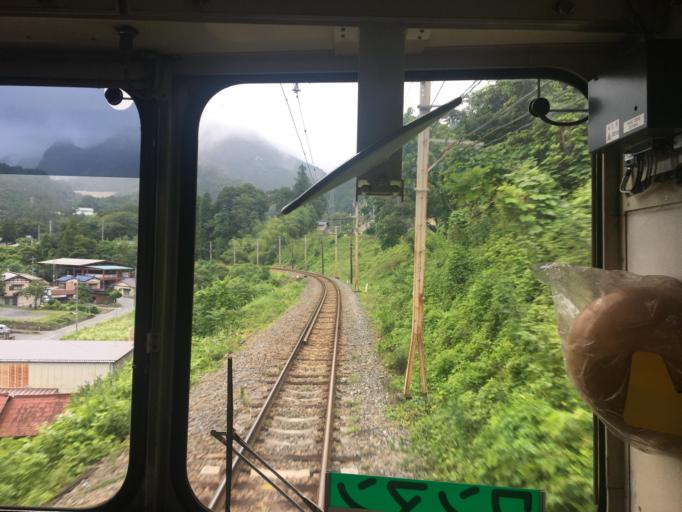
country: JP
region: Saitama
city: Chichibu
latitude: 35.9649
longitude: 139.0512
